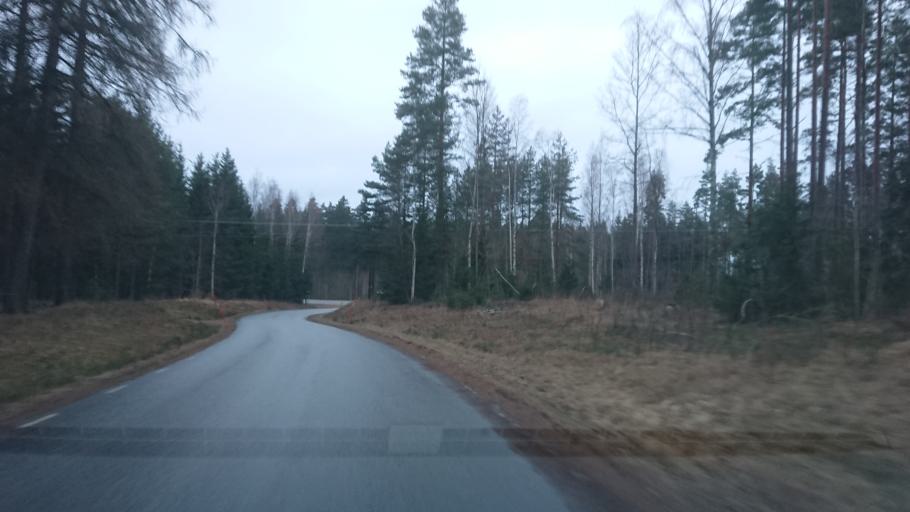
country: SE
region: Uppsala
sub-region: Osthammars Kommun
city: Bjorklinge
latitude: 60.0178
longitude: 17.5802
